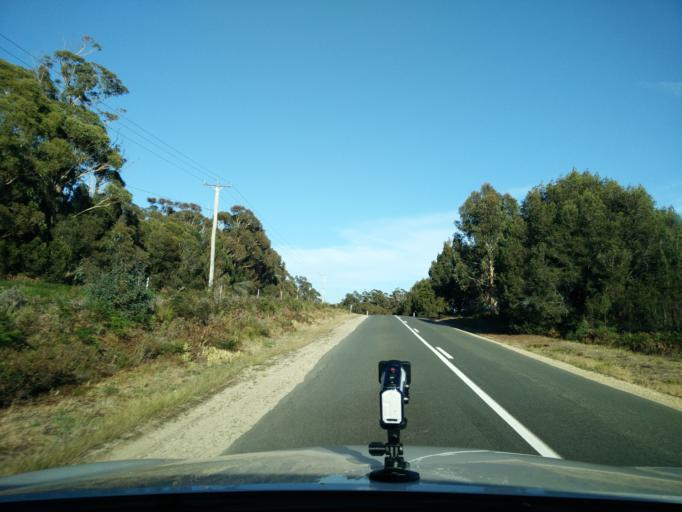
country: AU
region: Tasmania
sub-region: Break O'Day
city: St Helens
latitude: -41.2960
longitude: 148.1969
